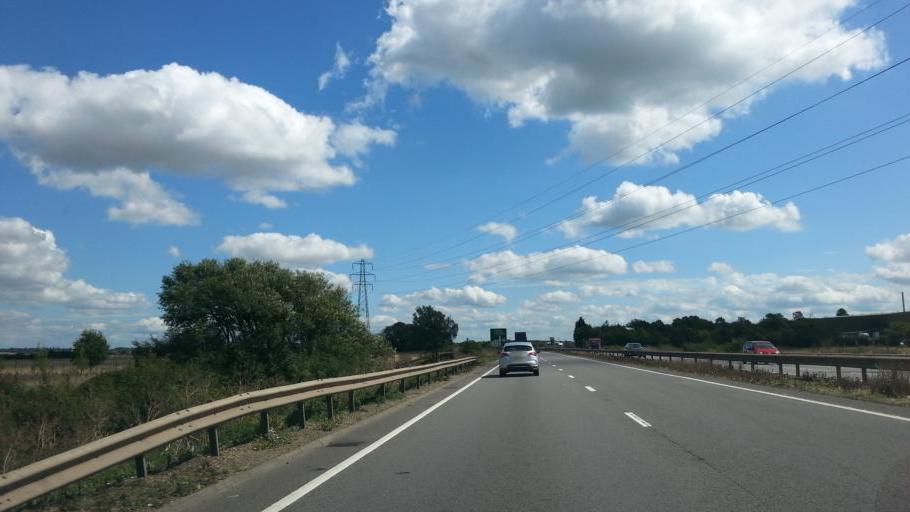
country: GB
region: England
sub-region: Cambridgeshire
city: Buckden
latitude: 52.3323
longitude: -0.2691
